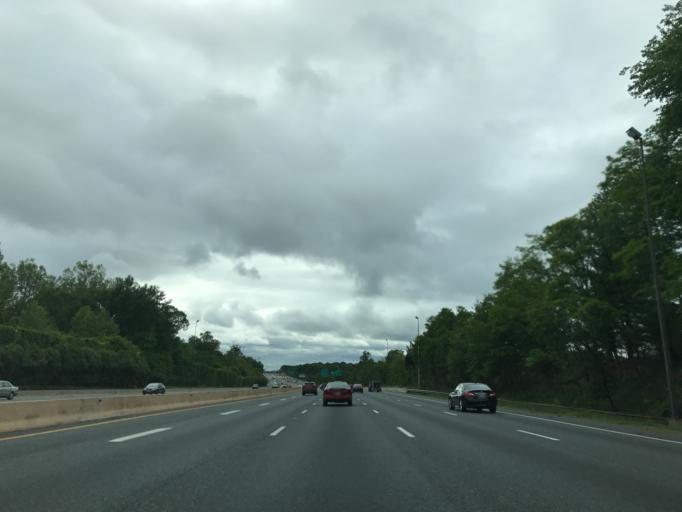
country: US
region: Maryland
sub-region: Prince George's County
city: Springdale
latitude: 38.9473
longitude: -76.8314
